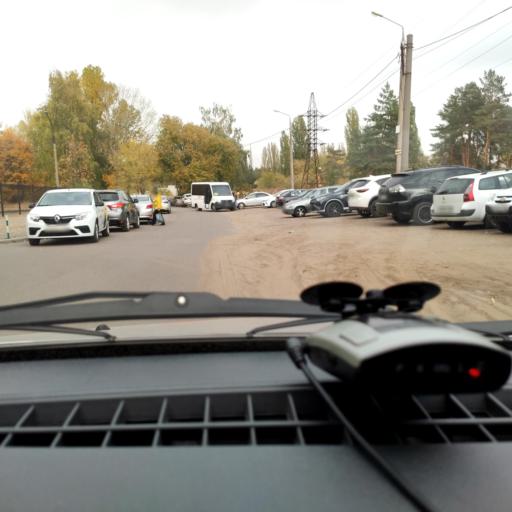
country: RU
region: Voronezj
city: Podgornoye
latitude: 51.7437
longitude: 39.1750
